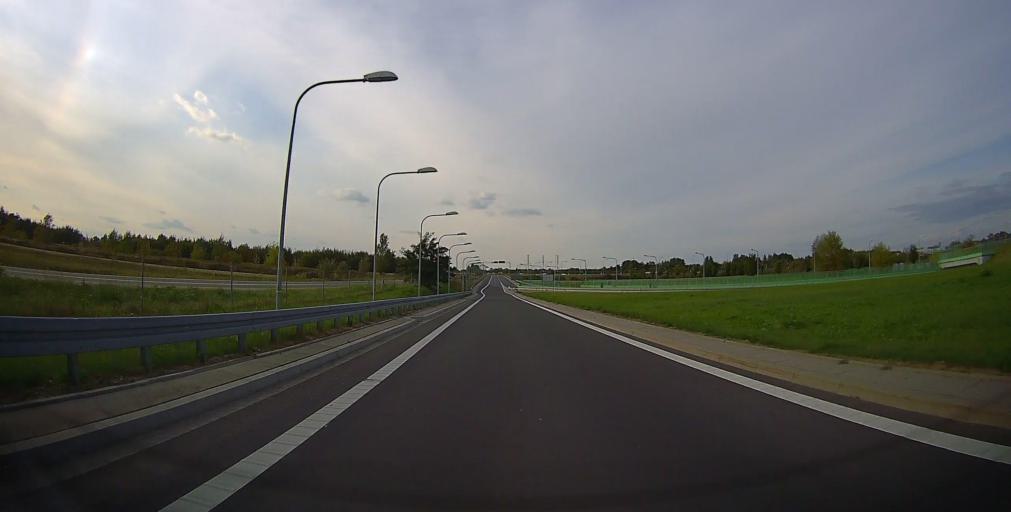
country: PL
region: Masovian Voivodeship
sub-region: Powiat piaseczynski
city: Mysiadlo
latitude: 52.1354
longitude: 20.9885
